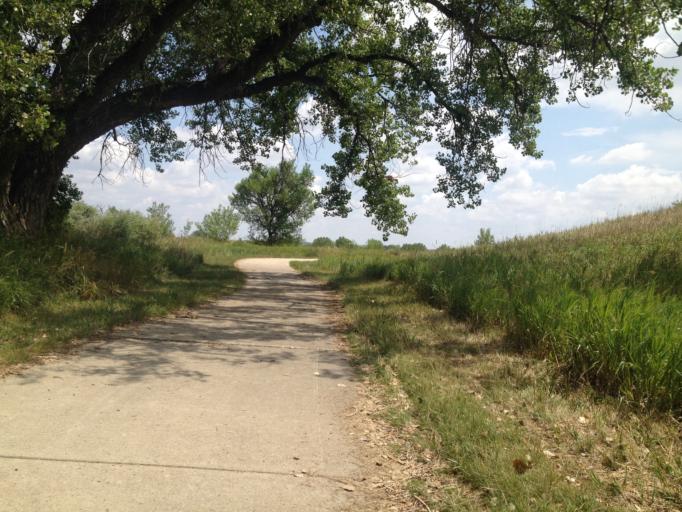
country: US
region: Colorado
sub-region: Boulder County
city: Louisville
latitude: 39.9717
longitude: -105.1473
